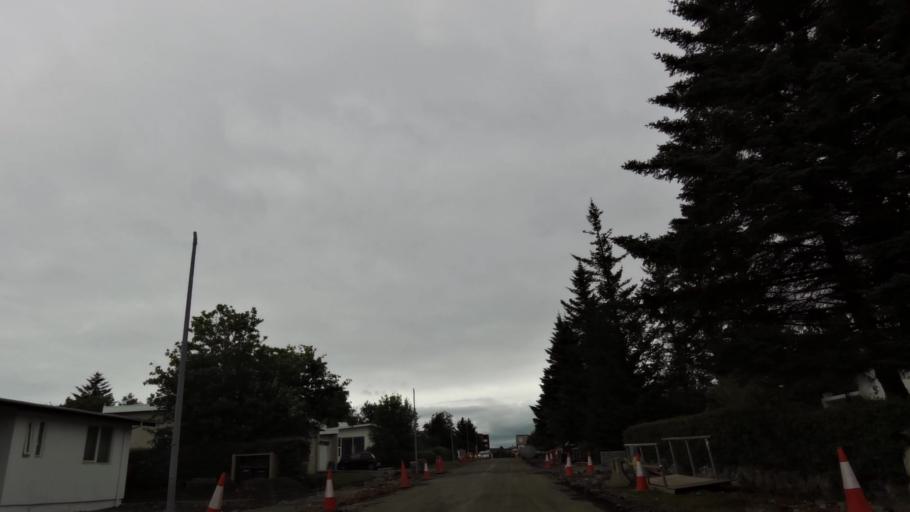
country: IS
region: Capital Region
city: Gardabaer
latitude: 64.0862
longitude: -21.9247
